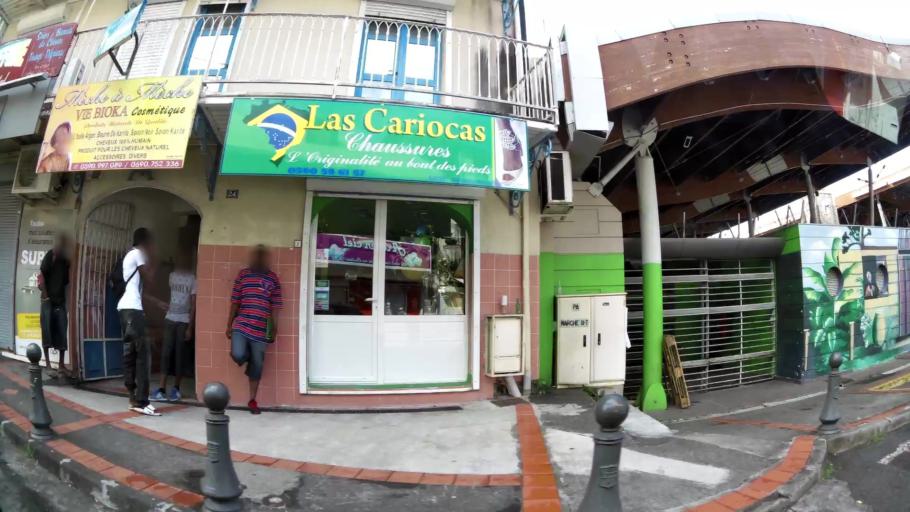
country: GP
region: Guadeloupe
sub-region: Guadeloupe
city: Basse-Terre
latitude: 15.9931
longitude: -61.7294
